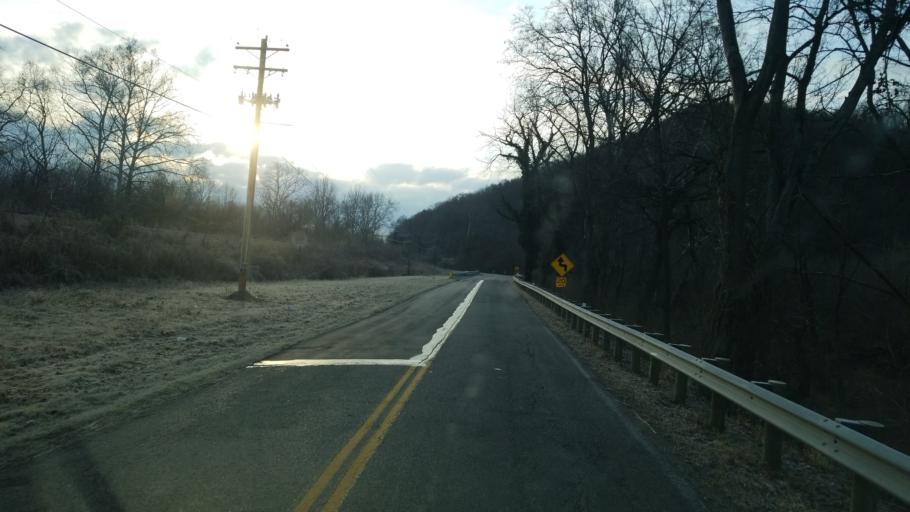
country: US
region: Ohio
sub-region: Ross County
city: Chillicothe
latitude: 39.2850
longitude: -82.9390
